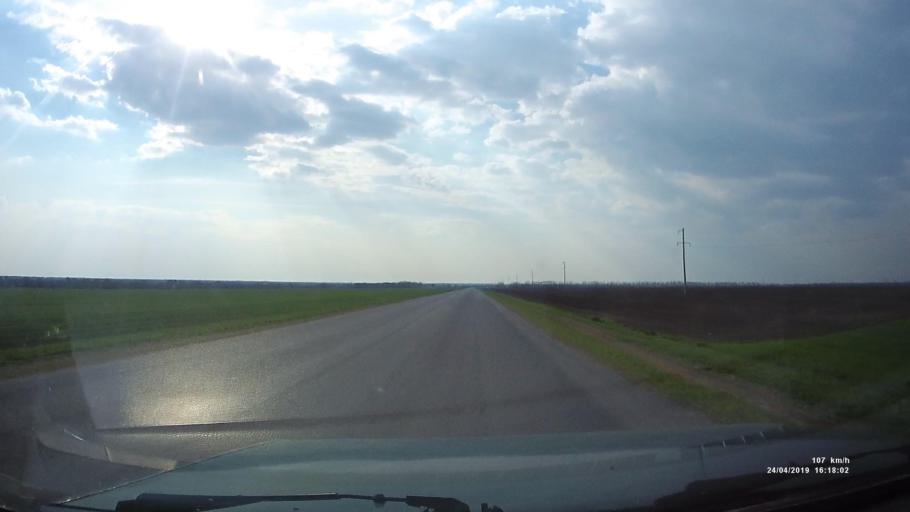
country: RU
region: Rostov
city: Sovetskoye
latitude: 46.7722
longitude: 42.1249
